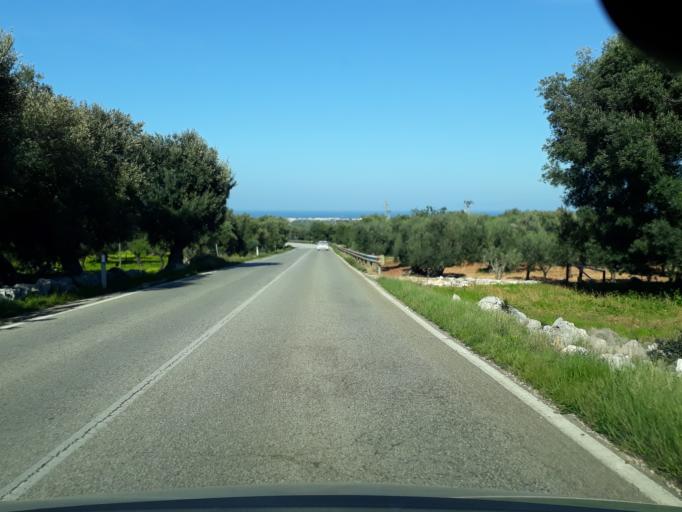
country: IT
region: Apulia
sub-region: Provincia di Bari
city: Monopoli
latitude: 40.9091
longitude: 17.2733
